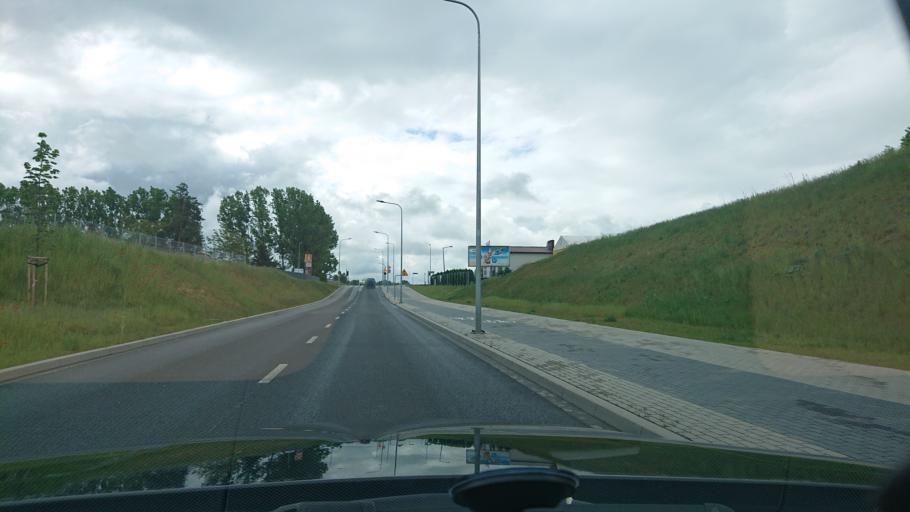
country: PL
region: Greater Poland Voivodeship
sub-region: Powiat gnieznienski
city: Gniezno
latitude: 52.5305
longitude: 17.6218
